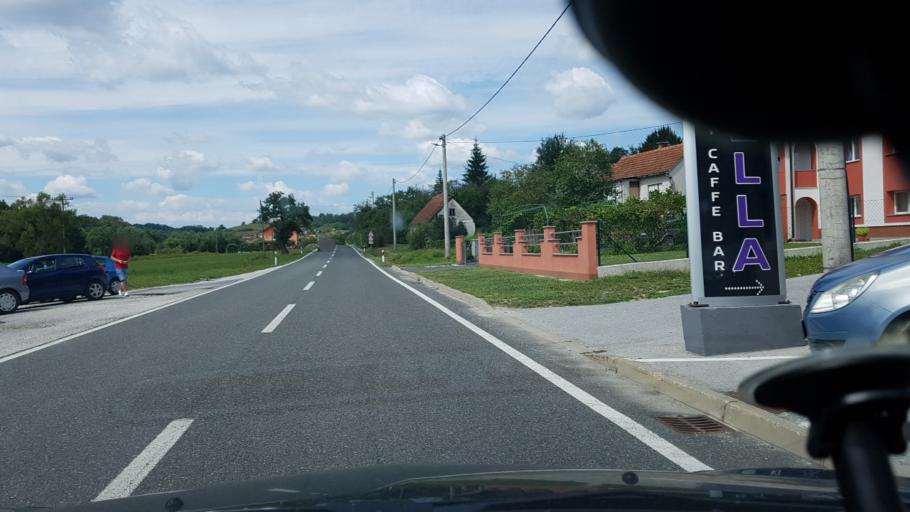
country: HR
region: Varazdinska
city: Lepoglava
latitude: 46.2216
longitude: 15.9948
